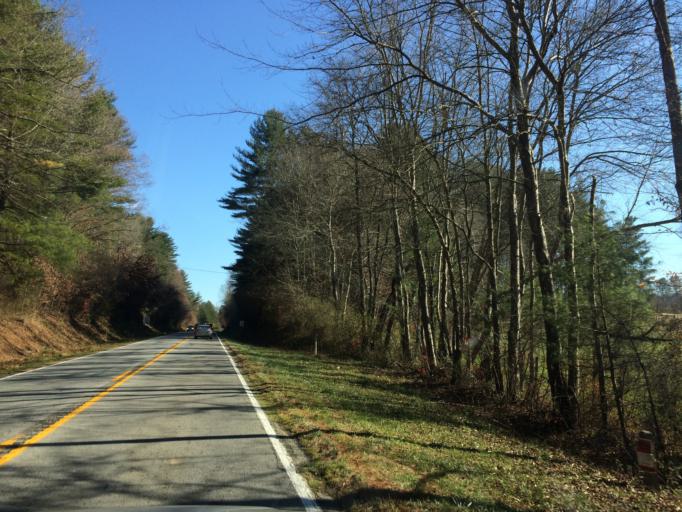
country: US
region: North Carolina
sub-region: Henderson County
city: Mountain Home
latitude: 35.3695
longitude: -82.5279
